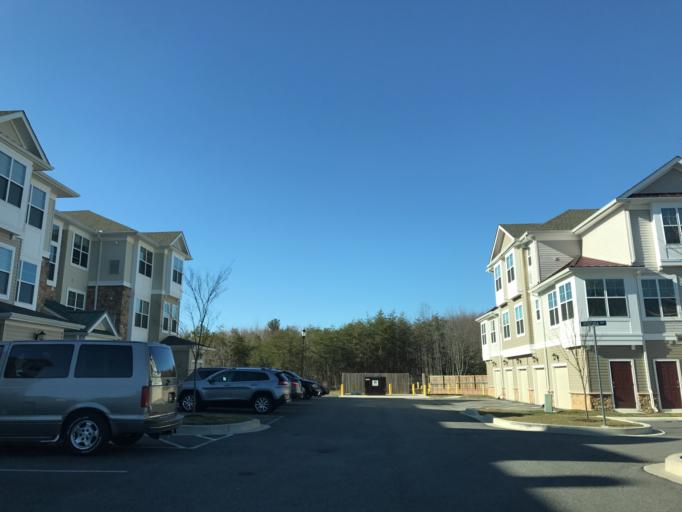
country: US
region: Maryland
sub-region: Harford County
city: Riverside
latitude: 39.4844
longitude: -76.2443
